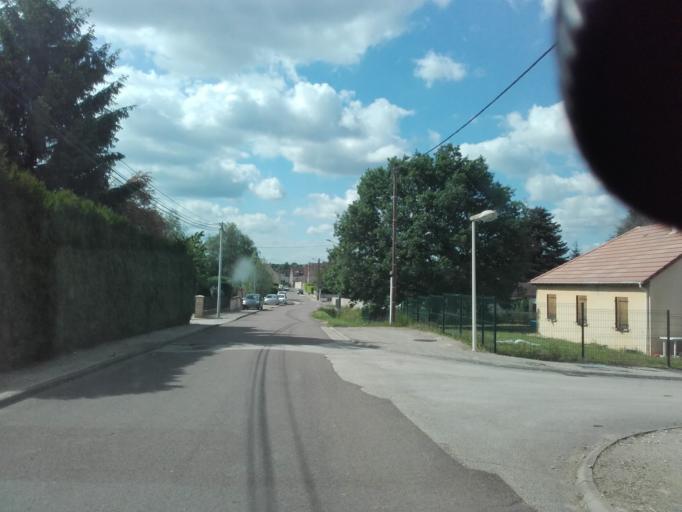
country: FR
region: Bourgogne
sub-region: Departement de Saone-et-Loire
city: Chagny
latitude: 46.8972
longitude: 4.7709
